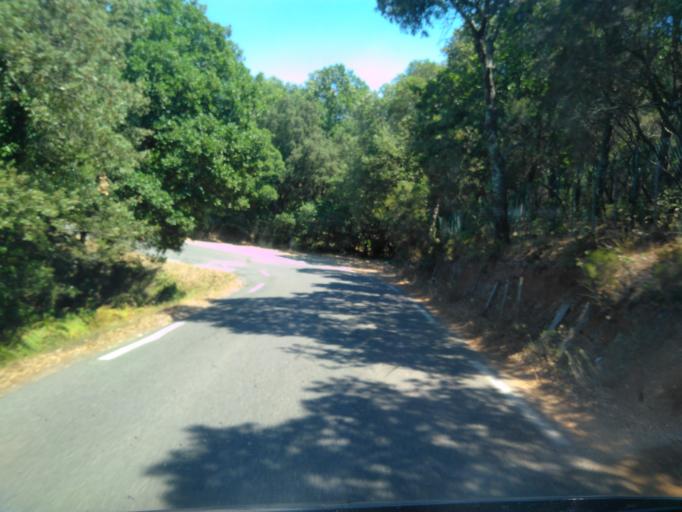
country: FR
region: Provence-Alpes-Cote d'Azur
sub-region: Departement du Var
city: Gassin
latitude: 43.2219
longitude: 6.5886
